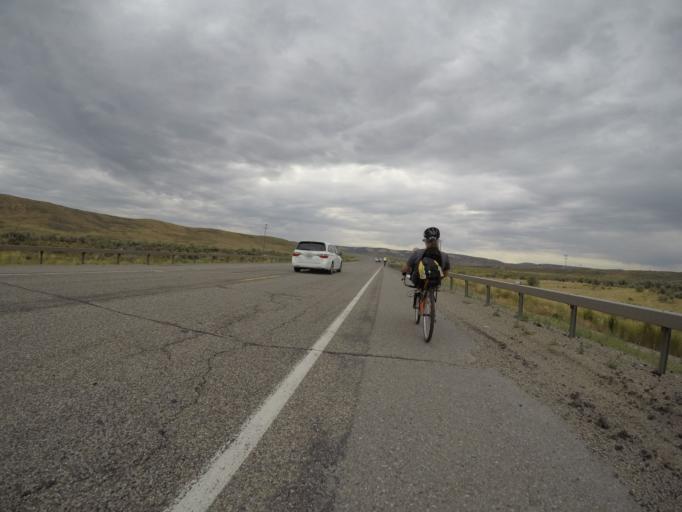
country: US
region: Wyoming
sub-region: Lincoln County
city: Kemmerer
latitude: 41.8108
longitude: -110.6968
